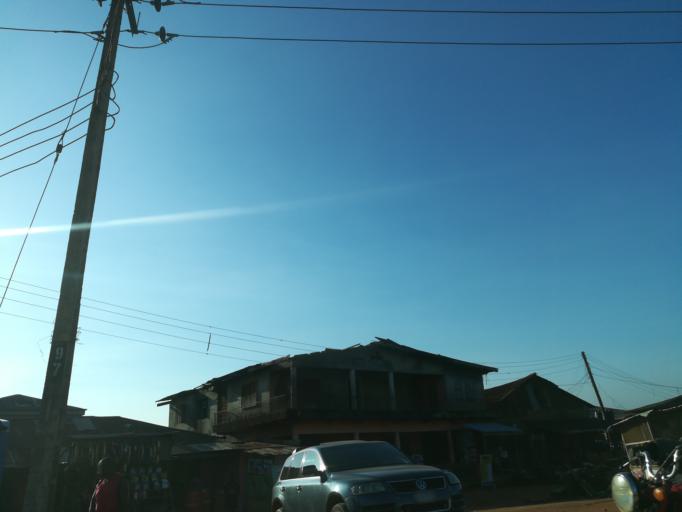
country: NG
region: Lagos
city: Ikorodu
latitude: 6.5903
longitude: 3.5172
